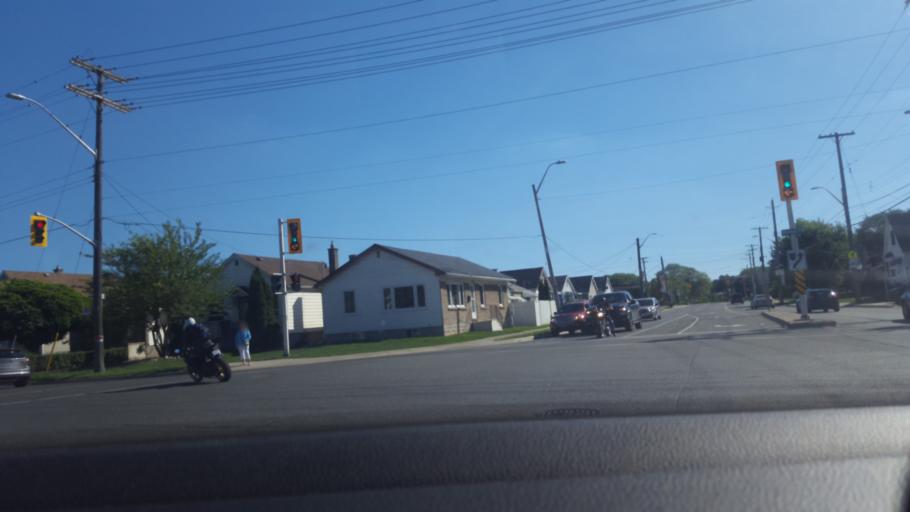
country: CA
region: Ontario
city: Hamilton
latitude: 43.2430
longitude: -79.7788
